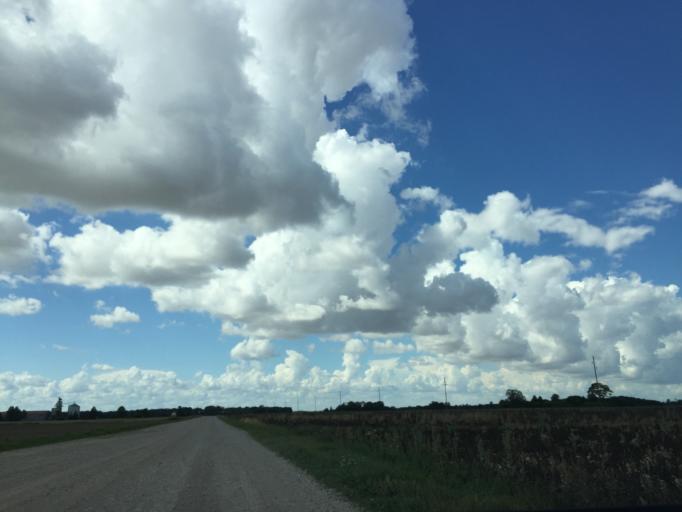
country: LV
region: Rundales
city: Pilsrundale
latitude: 56.3653
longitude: 24.0387
